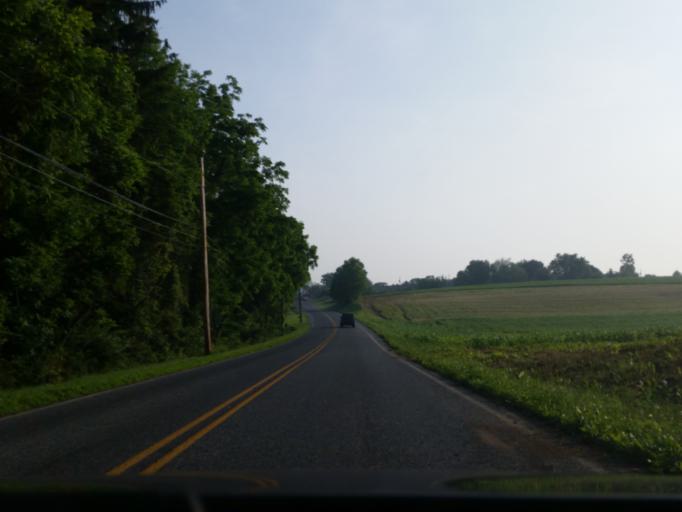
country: US
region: Pennsylvania
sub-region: Lebanon County
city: Annville
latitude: 40.3448
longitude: -76.5018
